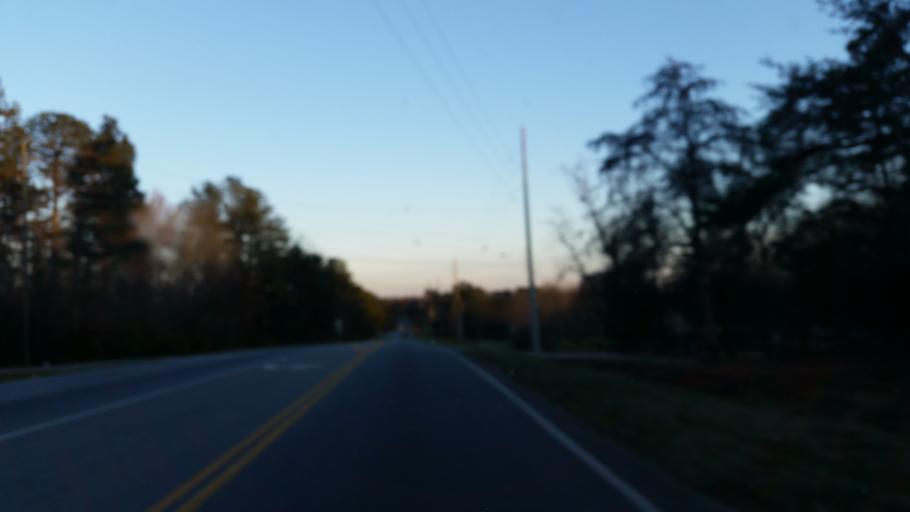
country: US
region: Georgia
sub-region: Hall County
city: Oakwood
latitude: 34.3197
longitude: -84.0032
